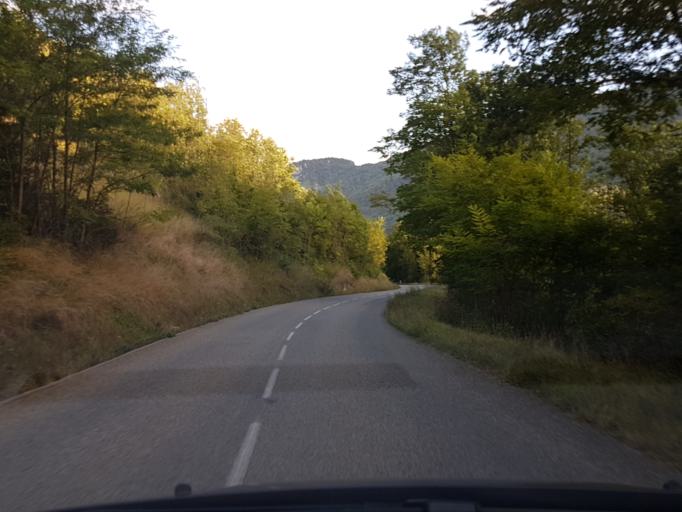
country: FR
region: Midi-Pyrenees
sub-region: Departement de l'Ariege
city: Tarascon-sur-Ariege
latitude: 42.8658
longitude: 1.5695
